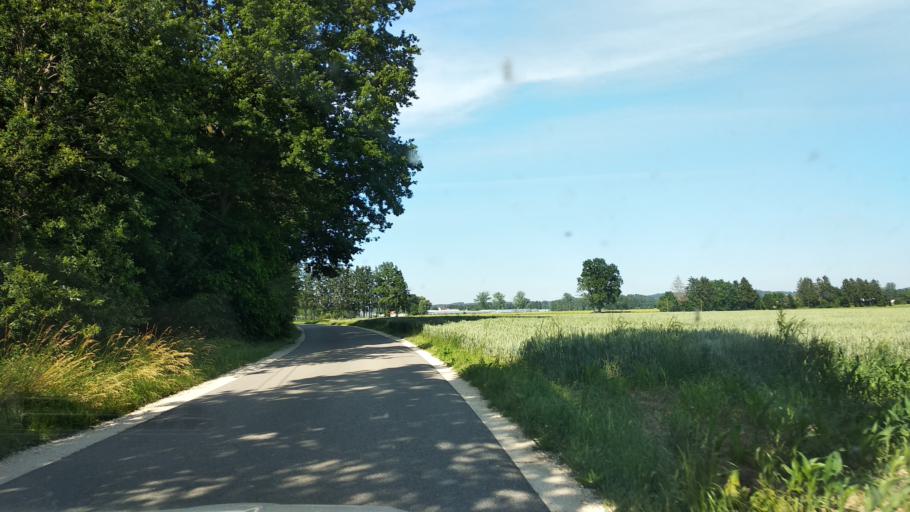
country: DE
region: Bavaria
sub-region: Swabia
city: Illertissen
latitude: 48.2355
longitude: 10.1270
